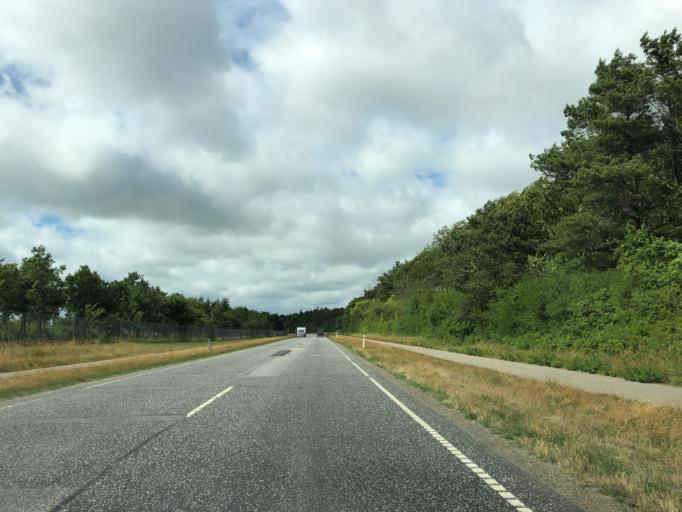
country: DK
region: Central Jutland
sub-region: Holstebro Kommune
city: Holstebro
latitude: 56.3456
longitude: 8.6094
